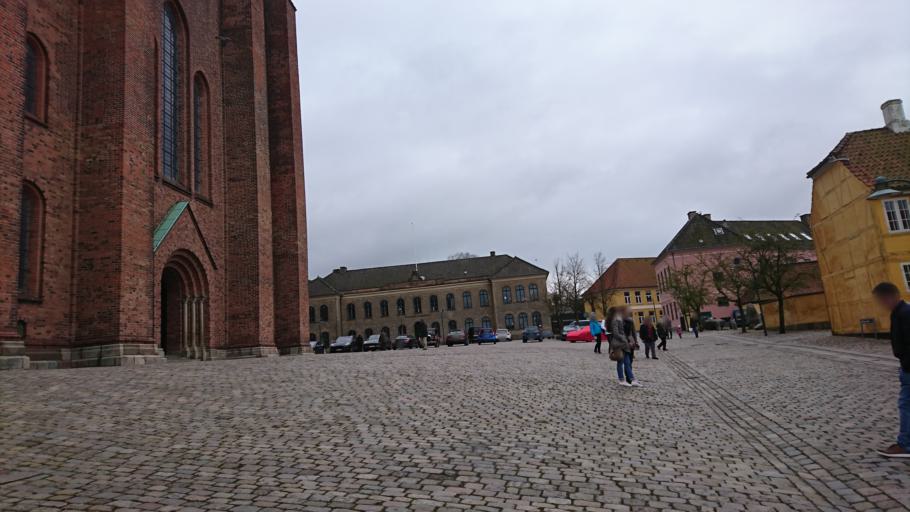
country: DK
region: Zealand
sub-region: Roskilde Kommune
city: Roskilde
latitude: 55.6430
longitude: 12.0795
